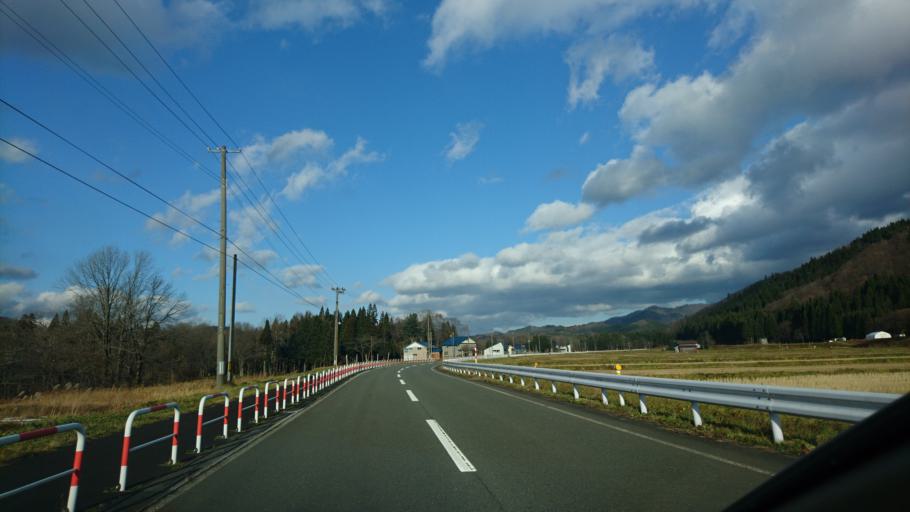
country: JP
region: Akita
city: Kakunodatemachi
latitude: 39.4455
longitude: 140.7716
